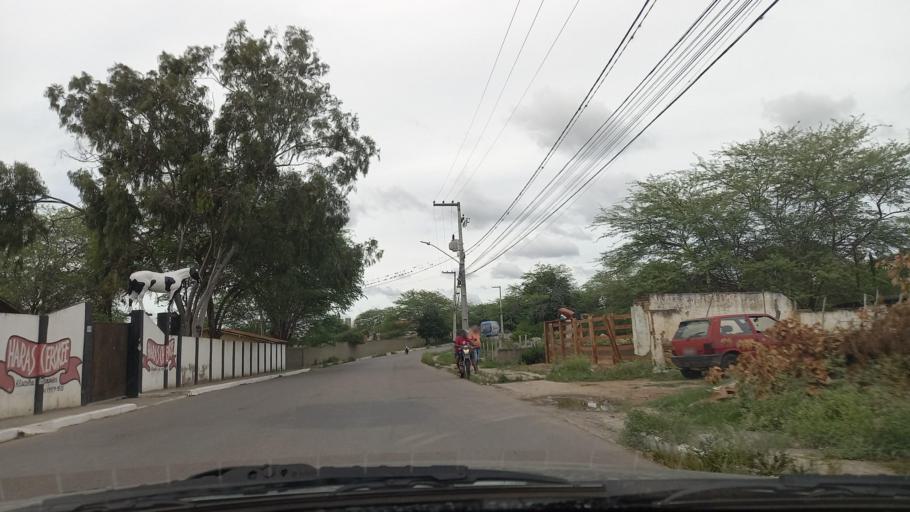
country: BR
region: Pernambuco
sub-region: Gravata
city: Gravata
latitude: -8.2065
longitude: -35.5848
